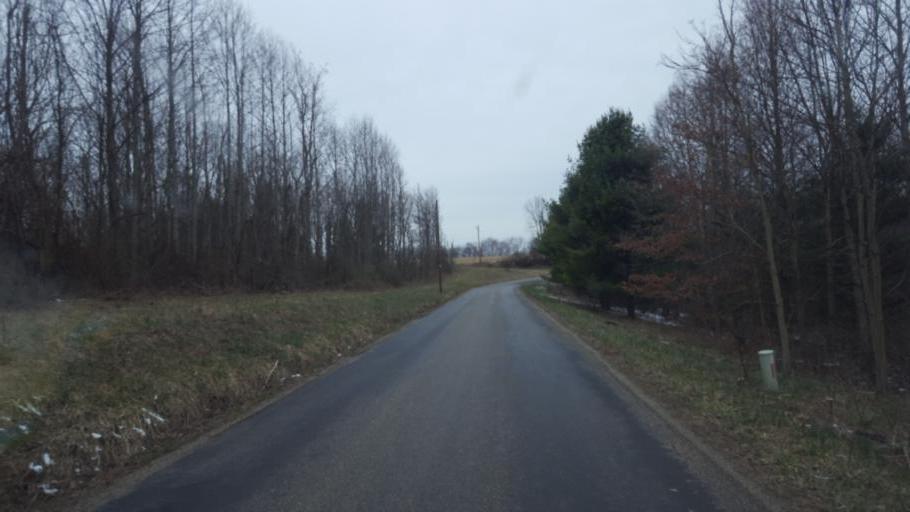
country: US
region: Ohio
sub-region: Sandusky County
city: Bellville
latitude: 40.5737
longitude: -82.4264
